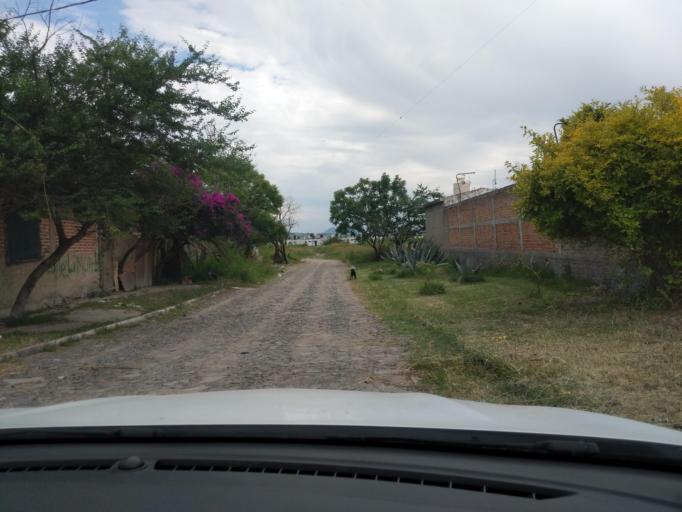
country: MX
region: Jalisco
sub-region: El Salto
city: Galaxia Bonito Jalisco
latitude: 20.5094
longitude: -103.1994
